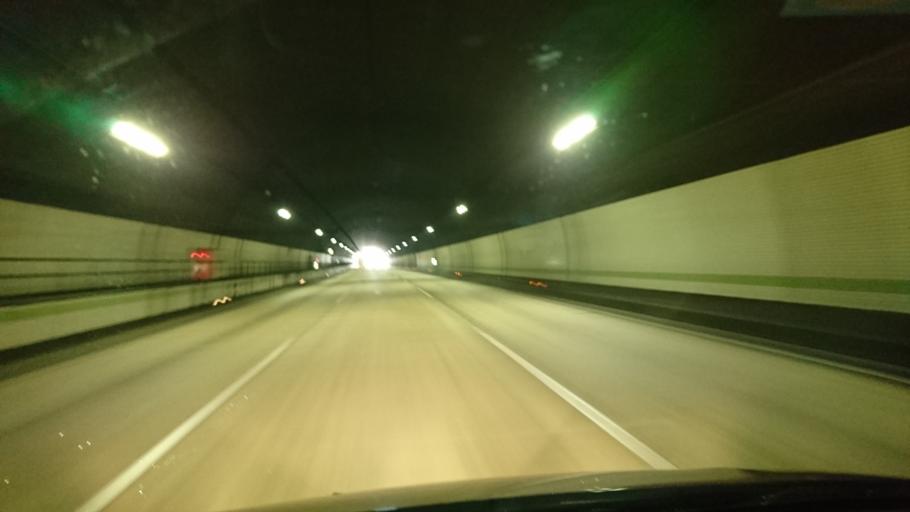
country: JP
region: Hyogo
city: Akashi
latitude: 34.6521
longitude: 135.0609
